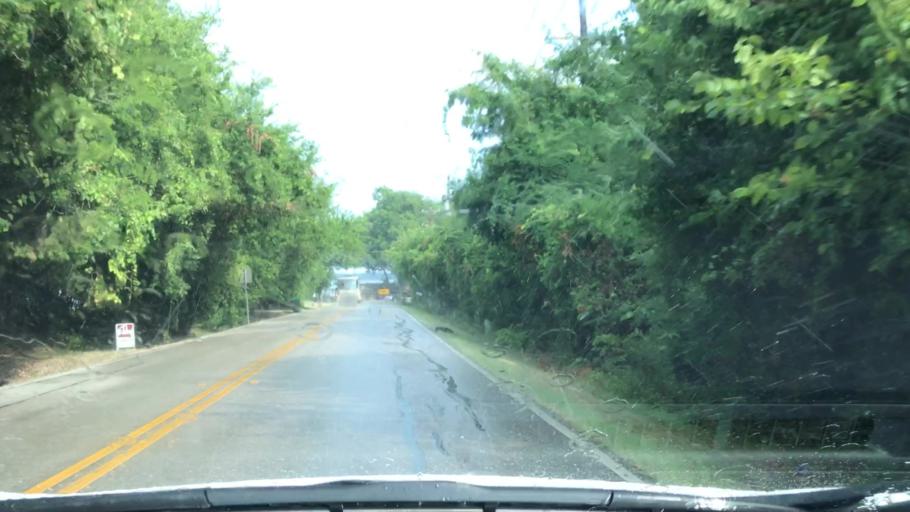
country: US
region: Texas
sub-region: Dallas County
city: Rowlett
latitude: 32.9523
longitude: -96.5216
